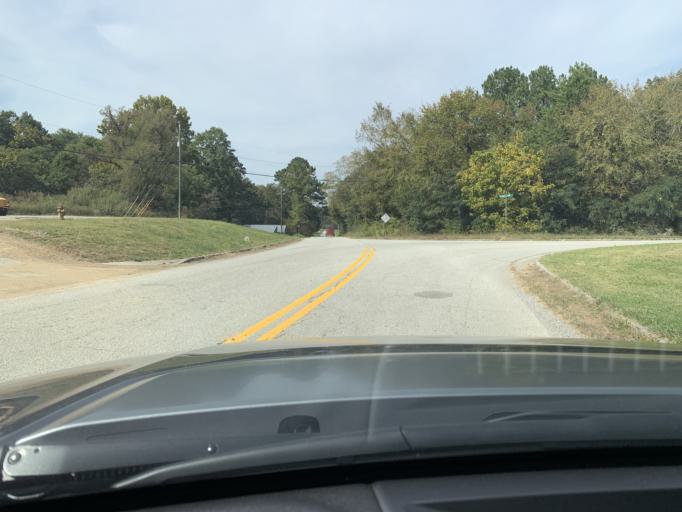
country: US
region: Georgia
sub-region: Polk County
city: Cedartown
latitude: 33.9713
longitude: -85.2595
